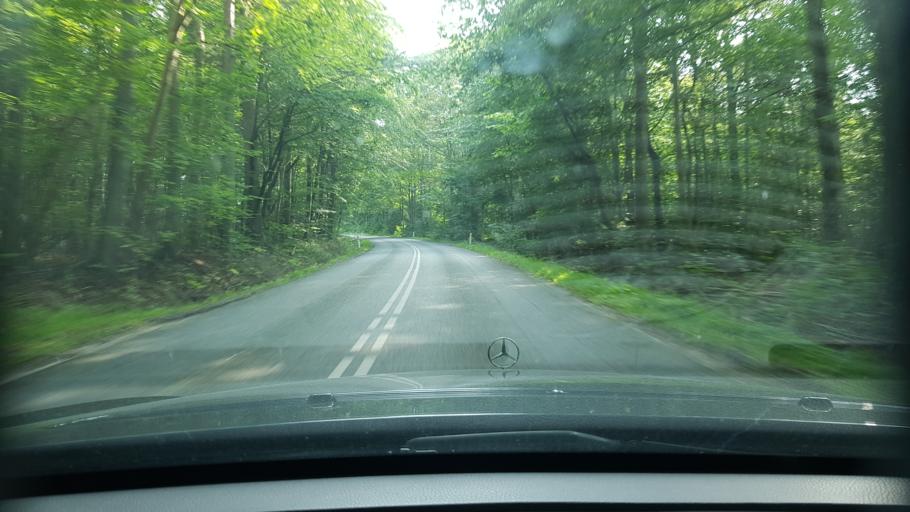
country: DK
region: North Denmark
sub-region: Mariagerfjord Kommune
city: Hadsund
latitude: 56.7500
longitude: 10.1793
